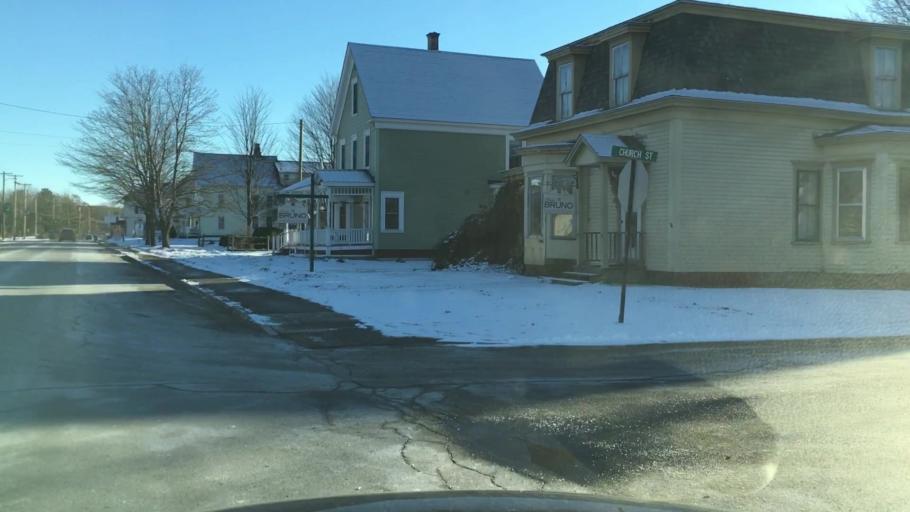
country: US
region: New Hampshire
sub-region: Grafton County
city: Woodsville
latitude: 44.1503
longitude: -72.0354
